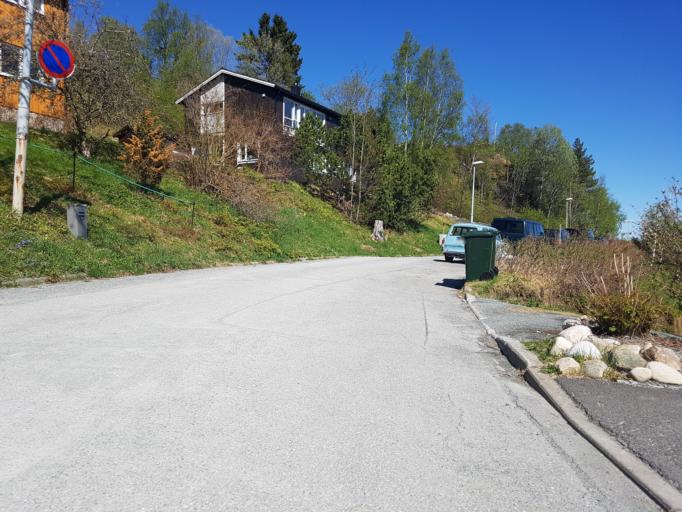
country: NO
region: Sor-Trondelag
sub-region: Trondheim
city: Trondheim
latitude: 63.4259
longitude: 10.3443
